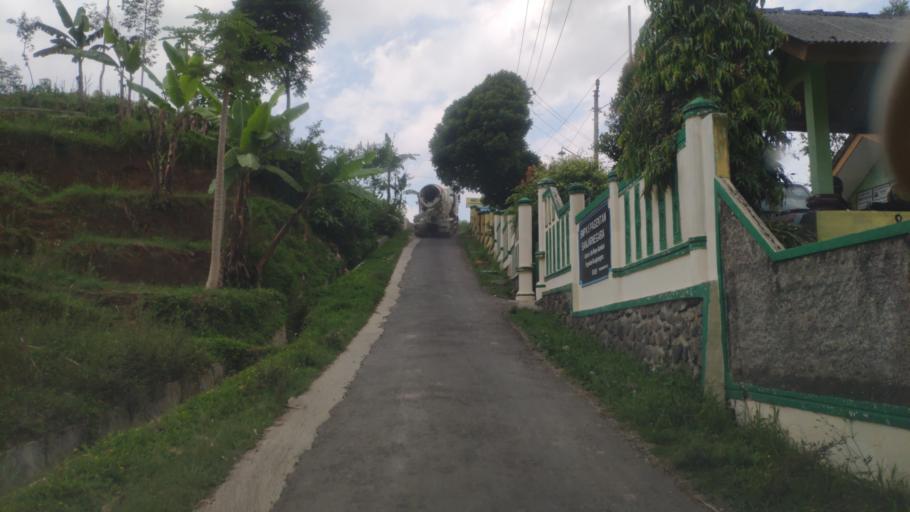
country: ID
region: Central Java
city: Wonosobo
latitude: -7.2766
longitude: 109.7810
